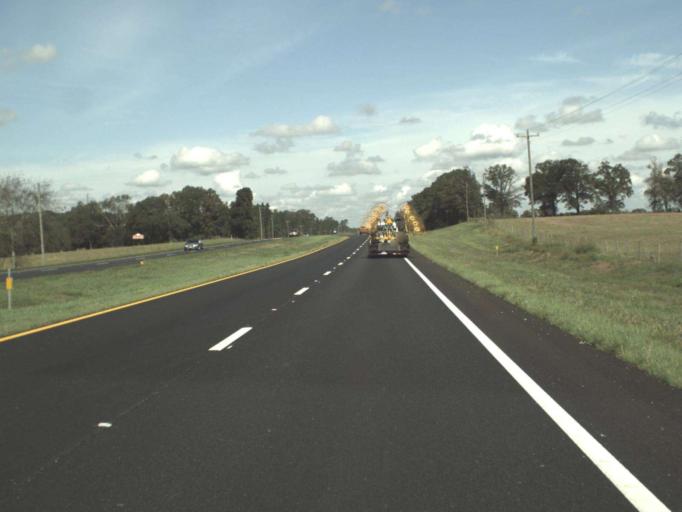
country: US
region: Florida
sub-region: Jackson County
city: Graceville
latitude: 30.8990
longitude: -85.3728
